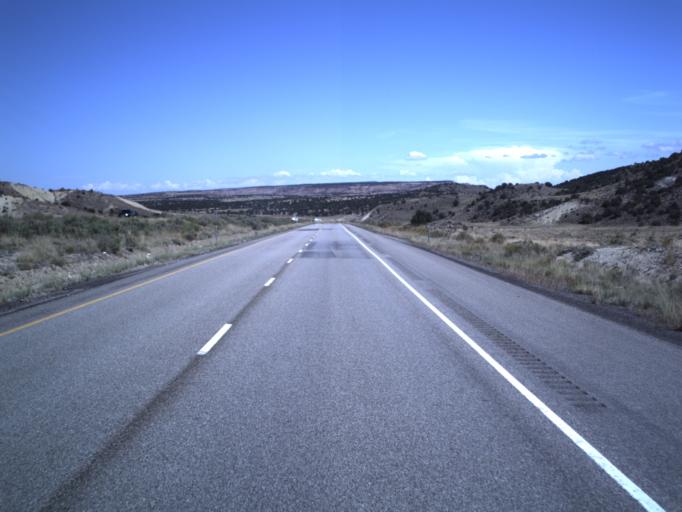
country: US
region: Utah
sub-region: Emery County
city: Ferron
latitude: 38.7923
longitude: -111.2932
